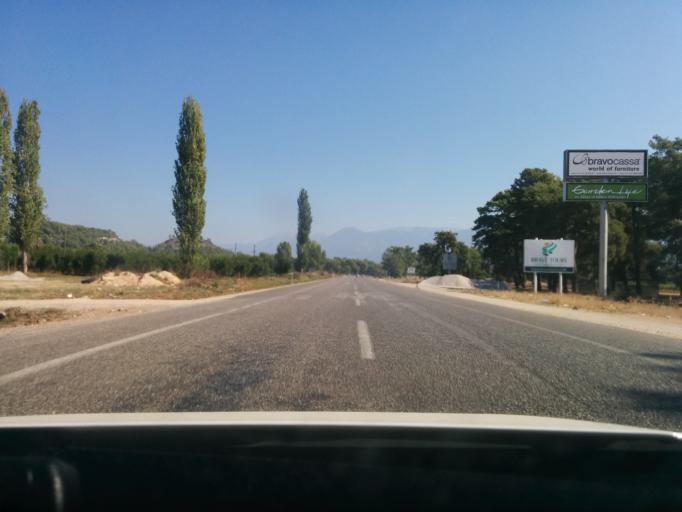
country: TR
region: Mugla
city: Esen
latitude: 36.4747
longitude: 29.3010
